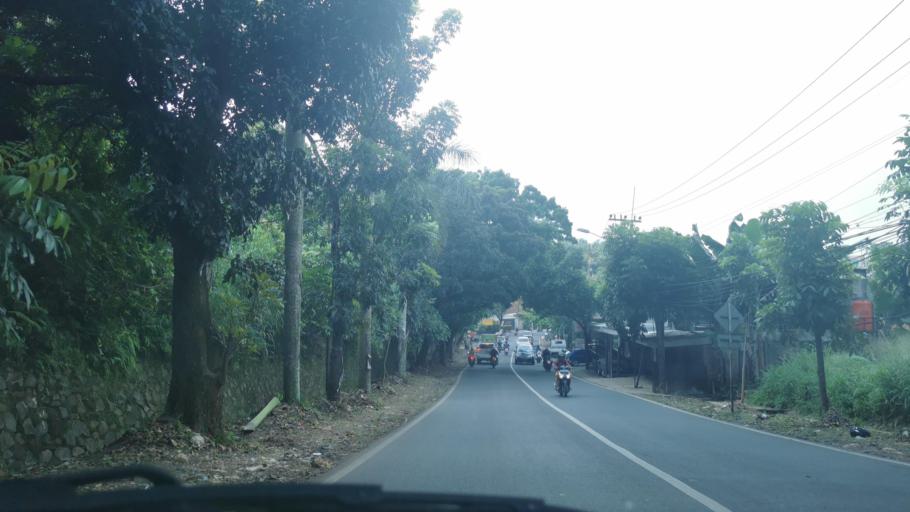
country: ID
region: West Java
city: Depok
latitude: -6.4088
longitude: 106.8322
